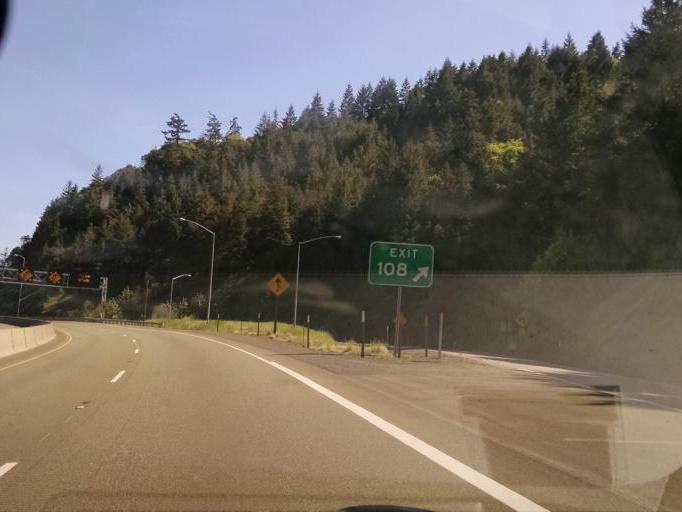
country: US
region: Oregon
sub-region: Douglas County
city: Myrtle Creek
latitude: 43.0271
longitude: -123.3008
